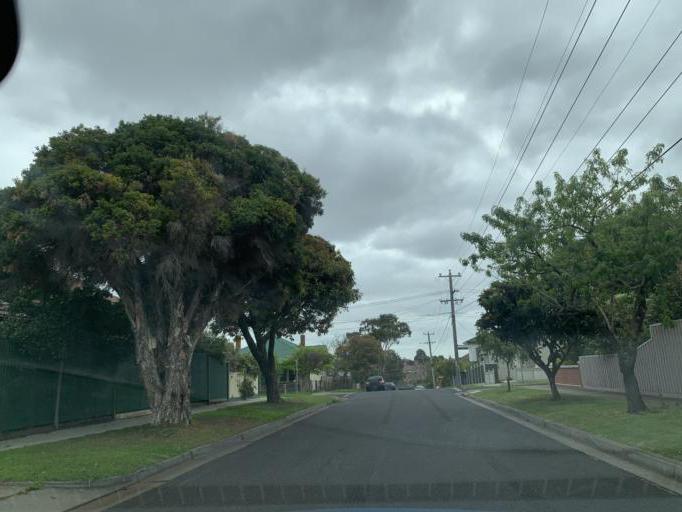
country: AU
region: Victoria
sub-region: Moreland
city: Pascoe Vale South
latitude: -37.7482
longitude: 144.9416
